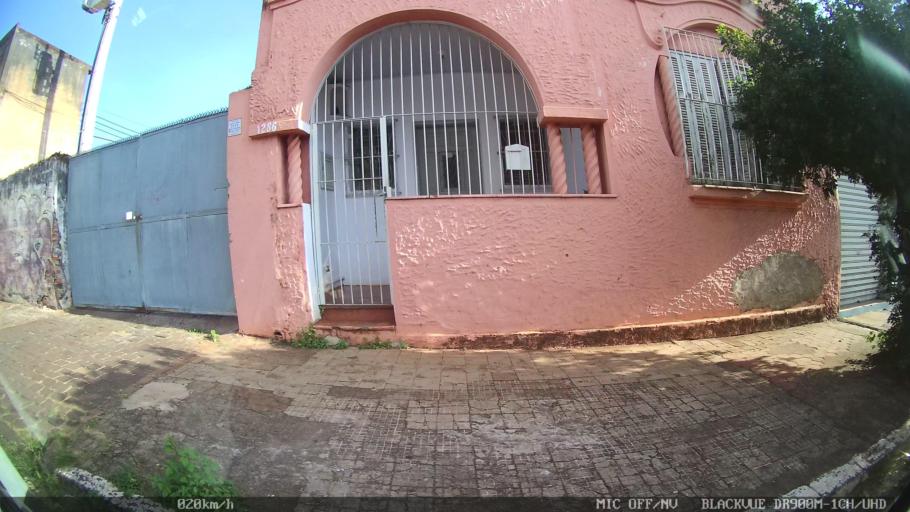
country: BR
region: Sao Paulo
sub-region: Ribeirao Preto
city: Ribeirao Preto
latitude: -21.1678
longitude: -47.8044
